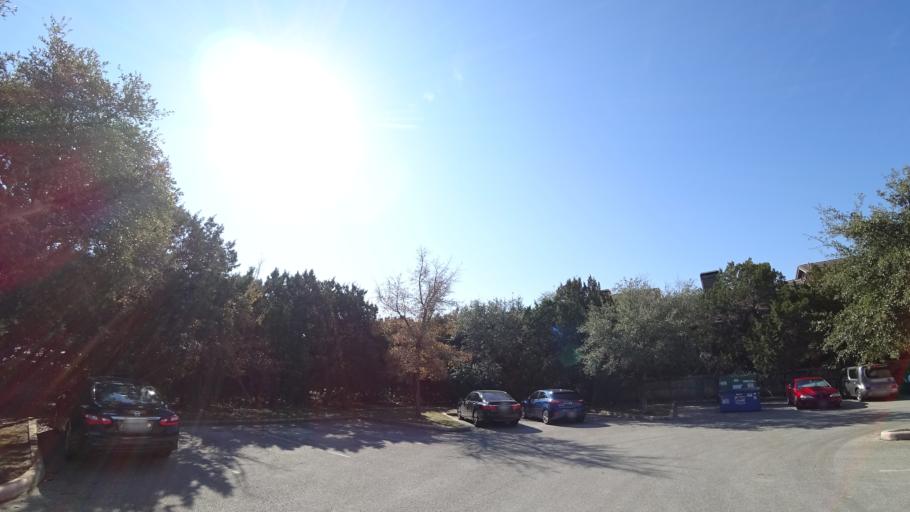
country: US
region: Texas
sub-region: Williamson County
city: Jollyville
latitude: 30.3749
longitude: -97.7622
